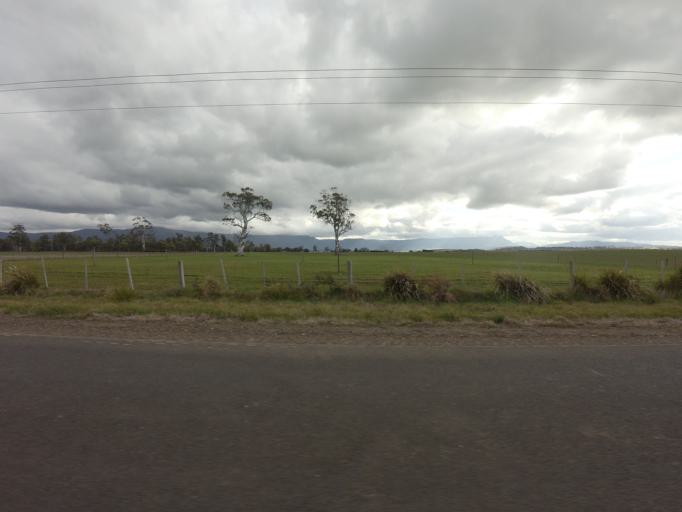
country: AU
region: Tasmania
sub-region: Northern Midlands
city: Longford
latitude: -41.7626
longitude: 147.0833
